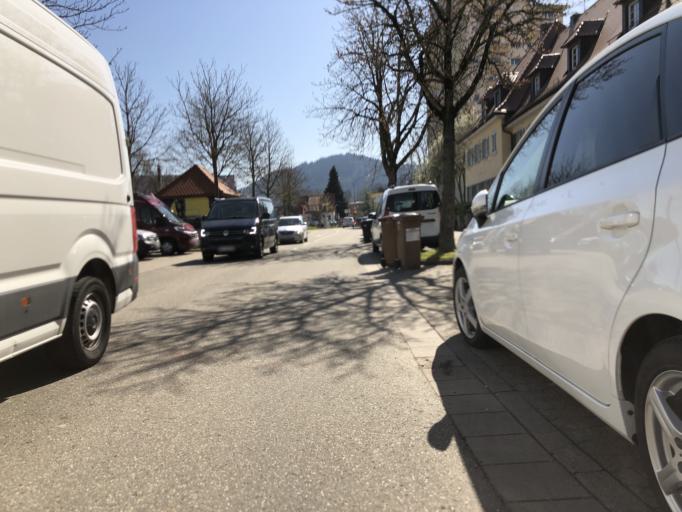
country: DE
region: Baden-Wuerttemberg
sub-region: Freiburg Region
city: Merzhausen
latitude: 47.9880
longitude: 7.8269
